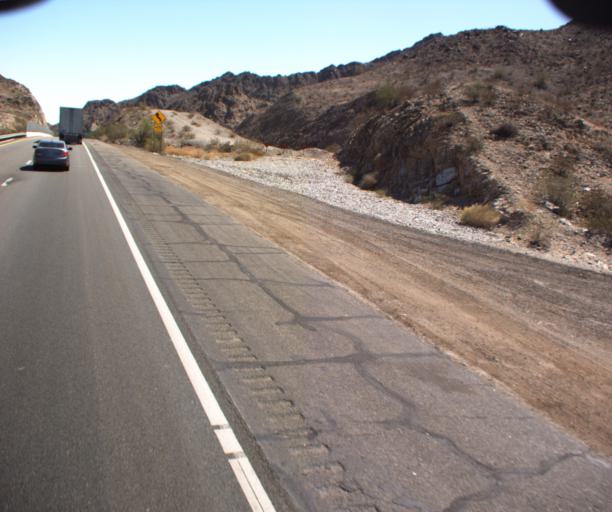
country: US
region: Arizona
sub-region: Yuma County
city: Fortuna Foothills
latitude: 32.6605
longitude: -114.3285
